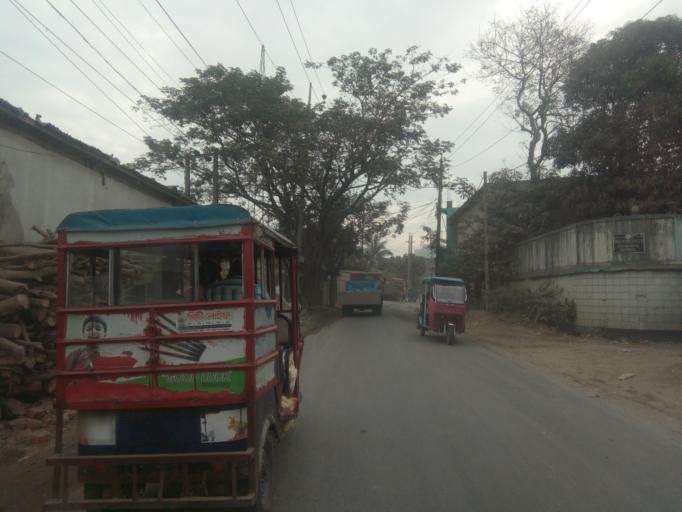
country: BD
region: Dhaka
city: Narayanganj
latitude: 23.5796
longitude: 90.5089
